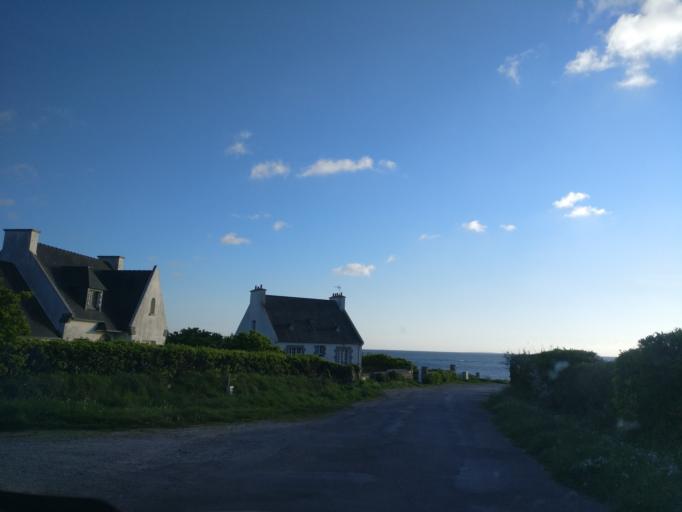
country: FR
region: Brittany
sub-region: Departement du Finistere
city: Porspoder
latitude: 48.4752
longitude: -4.7631
